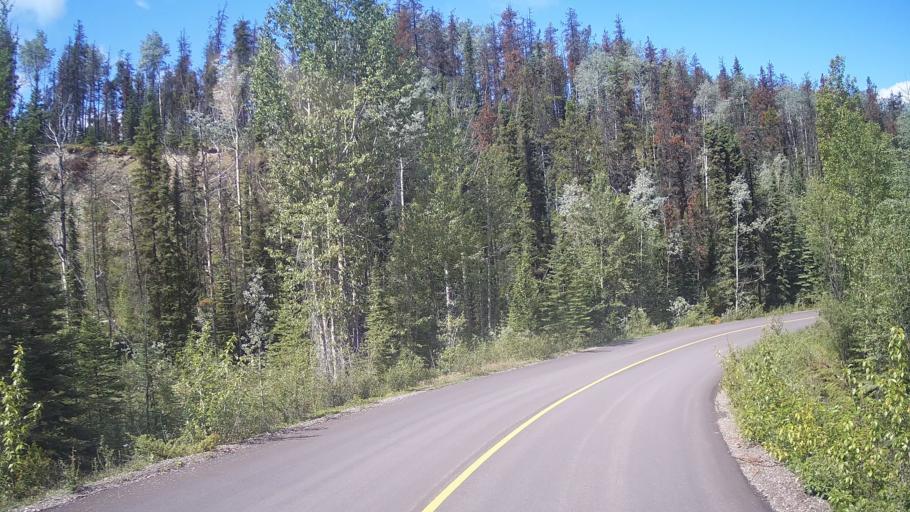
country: CA
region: Alberta
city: Jasper Park Lodge
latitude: 52.6630
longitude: -117.8859
